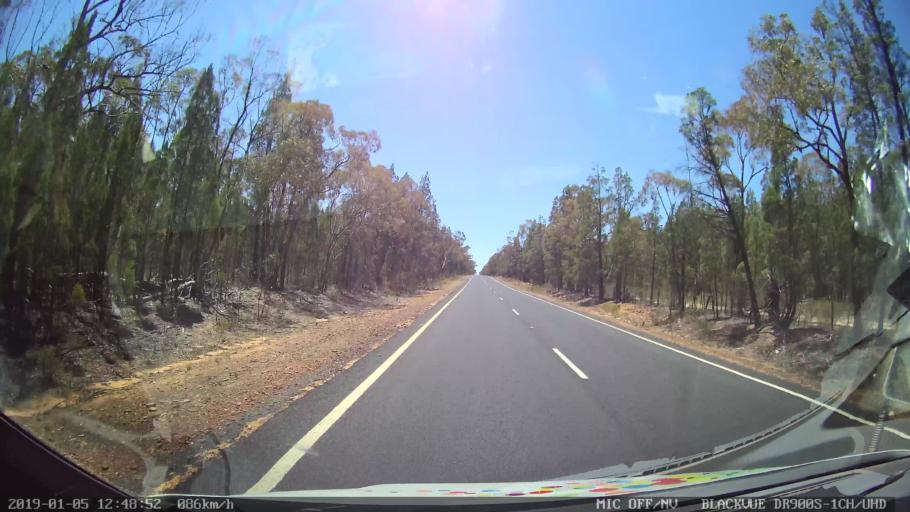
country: AU
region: New South Wales
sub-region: Warrumbungle Shire
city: Coonabarabran
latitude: -31.1179
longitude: 149.5985
